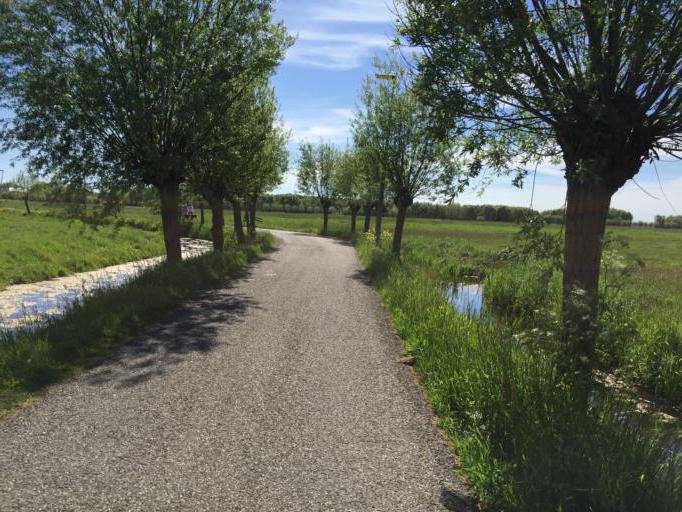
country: NL
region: South Holland
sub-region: Gemeente Vlaardingen
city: Vlaardingen
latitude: 51.9458
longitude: 4.3496
